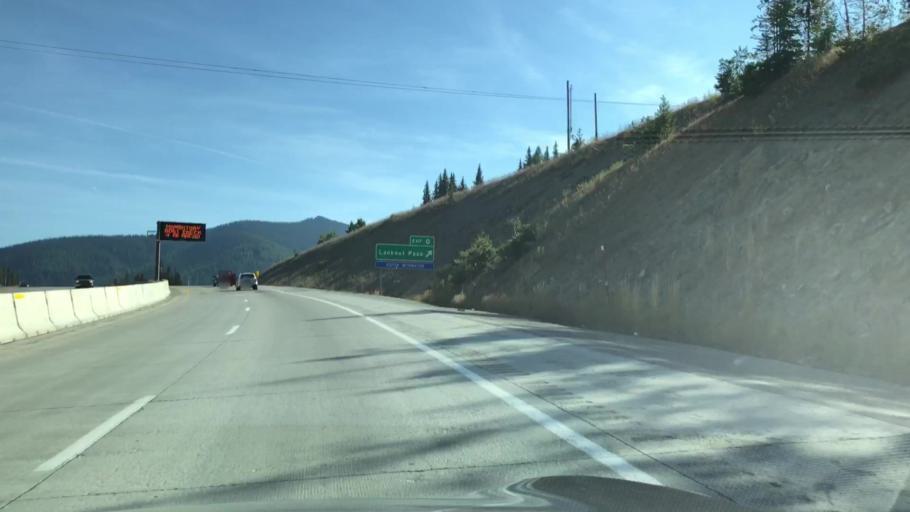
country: US
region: Idaho
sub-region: Shoshone County
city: Wallace
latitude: 47.4569
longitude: -115.6955
